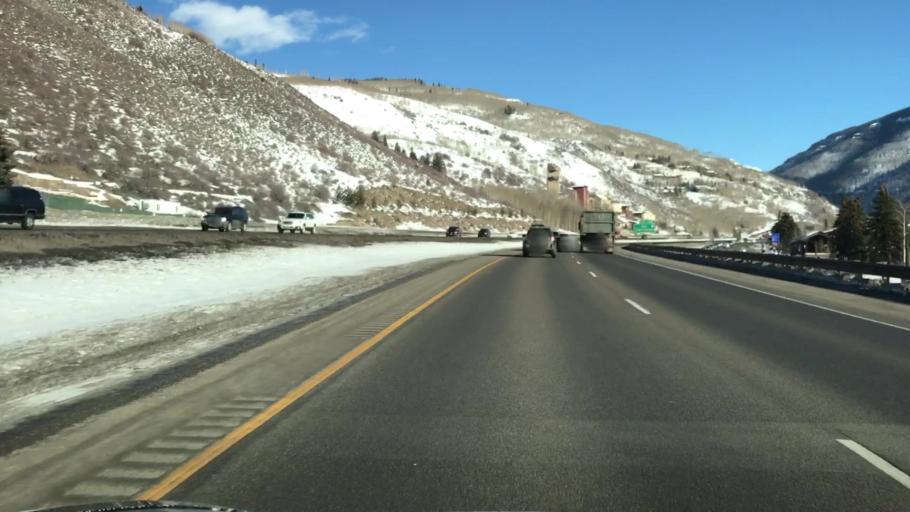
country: US
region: Colorado
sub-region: Eagle County
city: Vail
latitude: 39.6456
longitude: -106.3882
